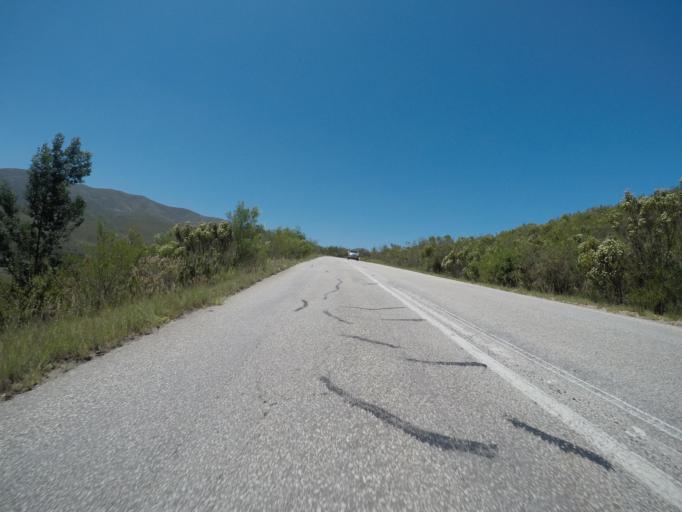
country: ZA
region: Eastern Cape
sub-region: Cacadu District Municipality
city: Kareedouw
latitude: -33.8848
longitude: 24.0737
